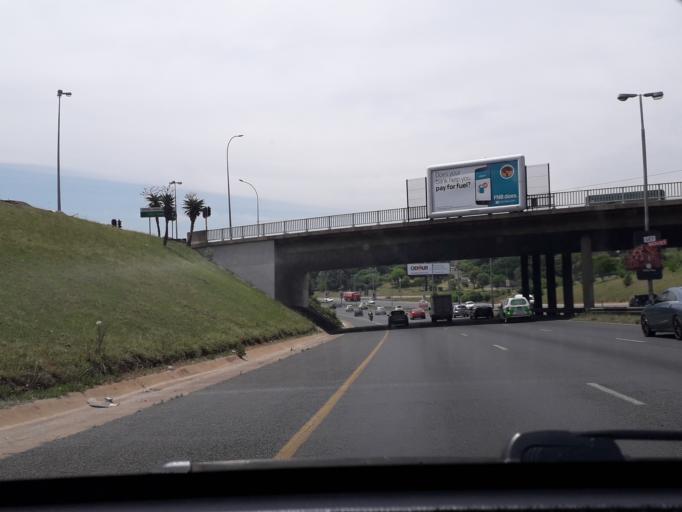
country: ZA
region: Gauteng
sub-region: City of Johannesburg Metropolitan Municipality
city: Johannesburg
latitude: -26.1394
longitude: 28.0666
